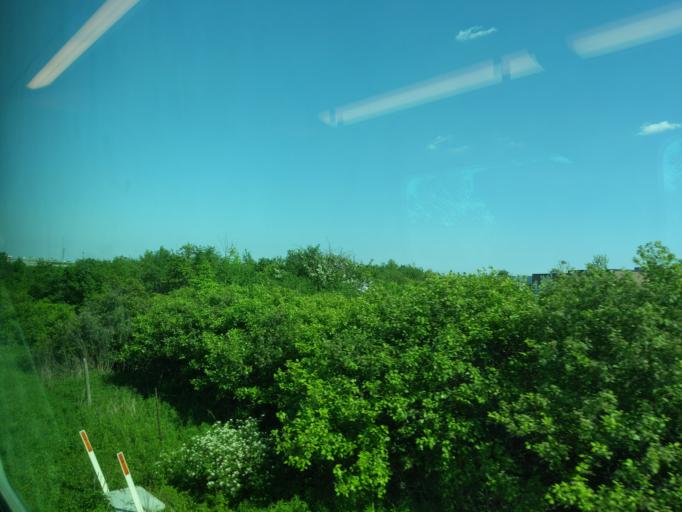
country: CA
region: Ontario
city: Etobicoke
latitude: 43.7051
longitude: -79.6203
